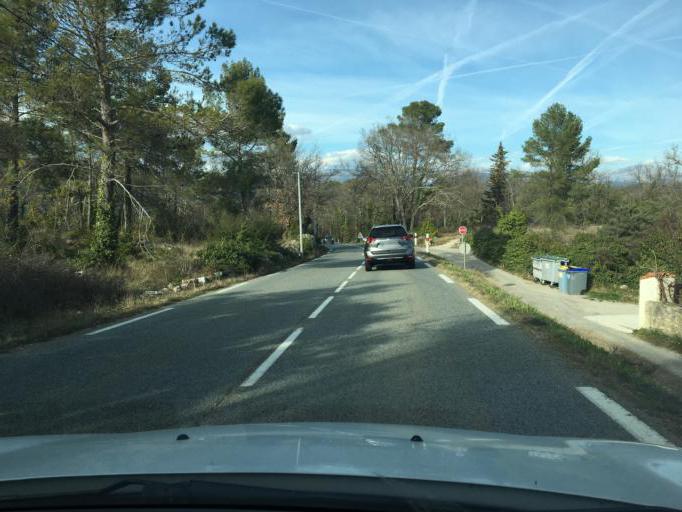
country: FR
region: Provence-Alpes-Cote d'Azur
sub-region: Departement du Var
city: Saint-Paul-en-Foret
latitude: 43.5924
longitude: 6.6825
